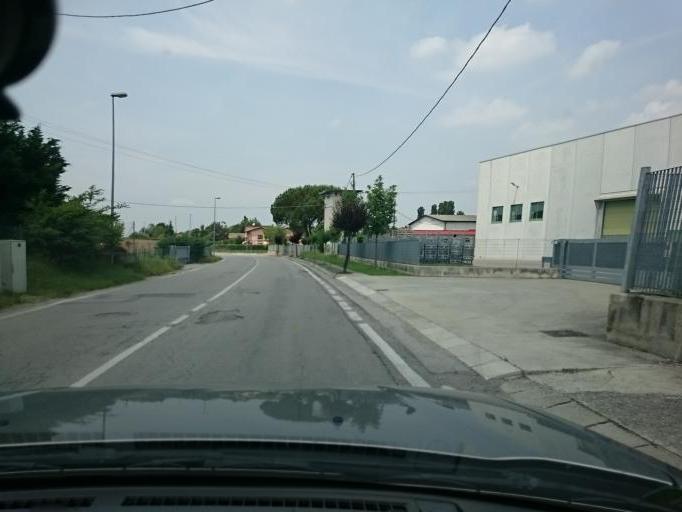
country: IT
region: Veneto
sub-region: Provincia di Padova
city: Sant'Angelo di Piove di Sacco
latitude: 45.3089
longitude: 11.9989
